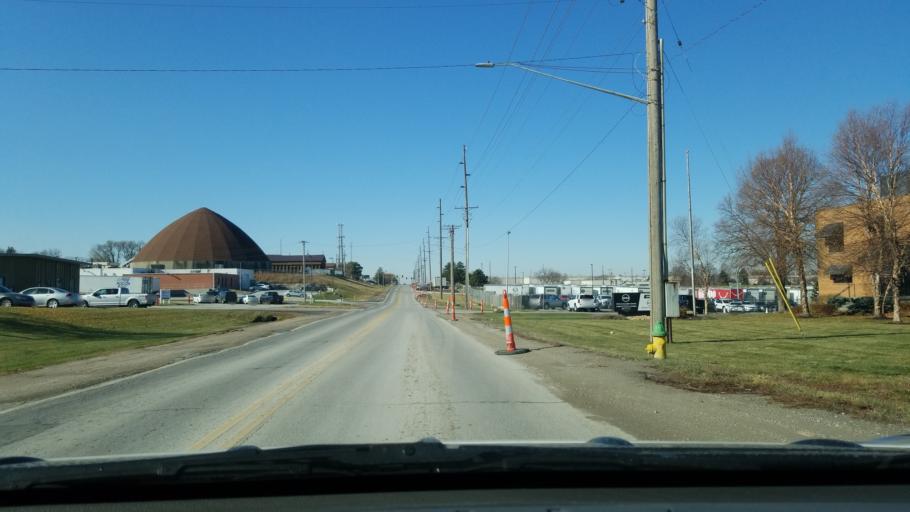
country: US
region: Nebraska
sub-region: Douglas County
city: Ralston
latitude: 41.2162
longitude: -96.0765
